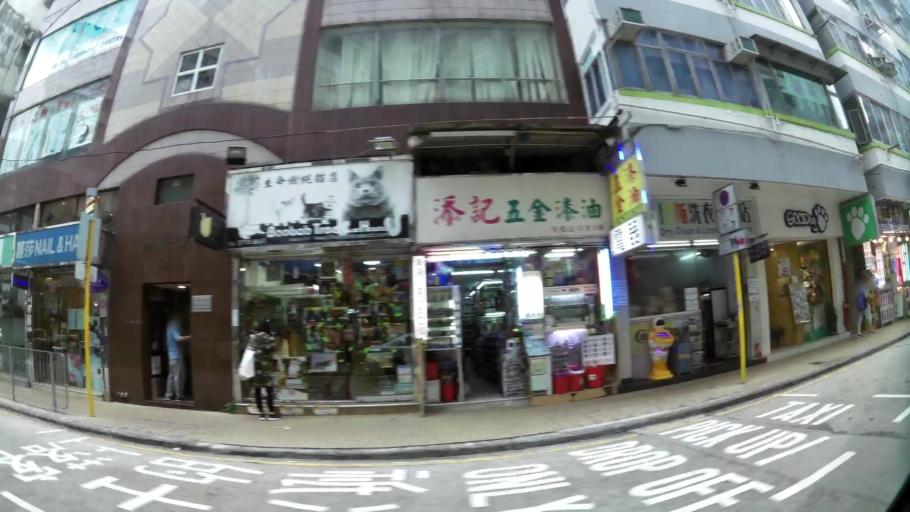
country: HK
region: Kowloon City
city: Kowloon
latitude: 22.3193
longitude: 114.1750
